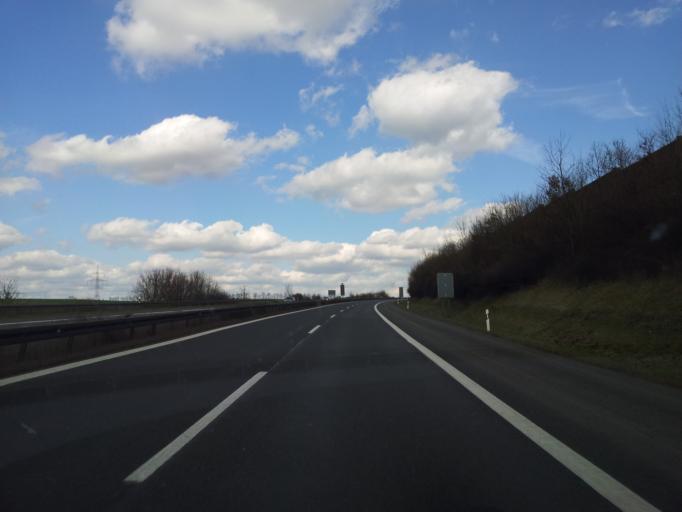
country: DE
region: Bavaria
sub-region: Upper Franconia
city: Memmelsdorf
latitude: 49.9492
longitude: 10.9707
